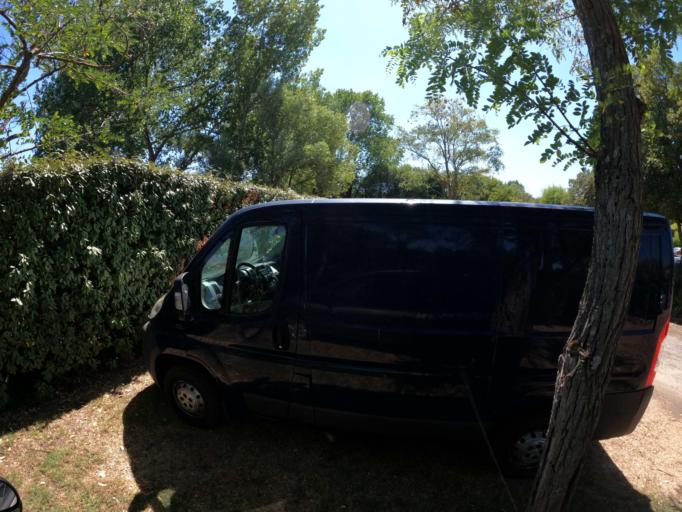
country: FR
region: Pays de la Loire
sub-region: Departement de la Vendee
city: Saint-Jean-de-Monts
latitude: 46.8076
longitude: -2.1038
